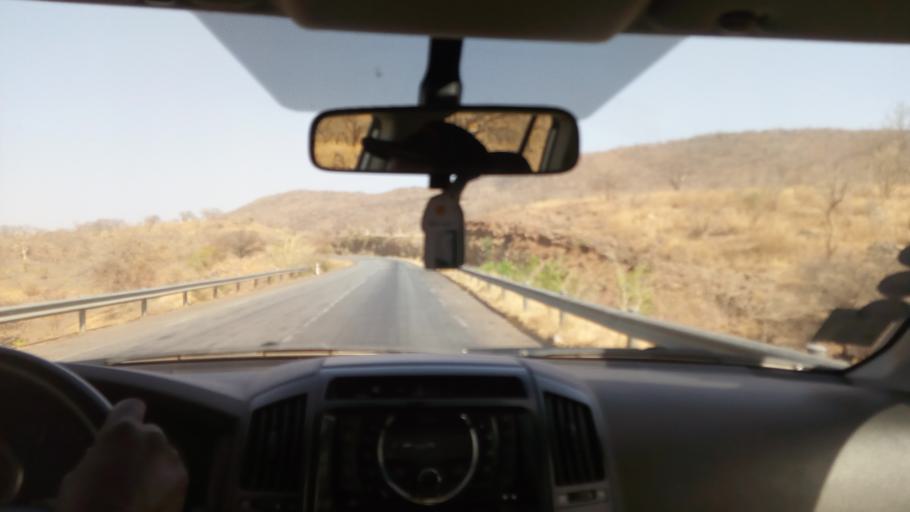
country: ML
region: Kayes
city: Yelimane
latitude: 14.6454
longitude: -10.6690
